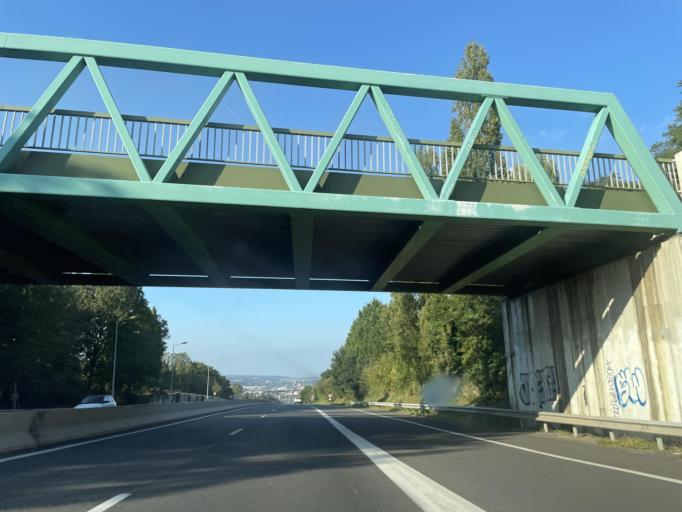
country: FR
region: Ile-de-France
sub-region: Departement de Seine-et-Marne
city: Nanteuil-les-Meaux
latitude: 48.9277
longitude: 2.8806
